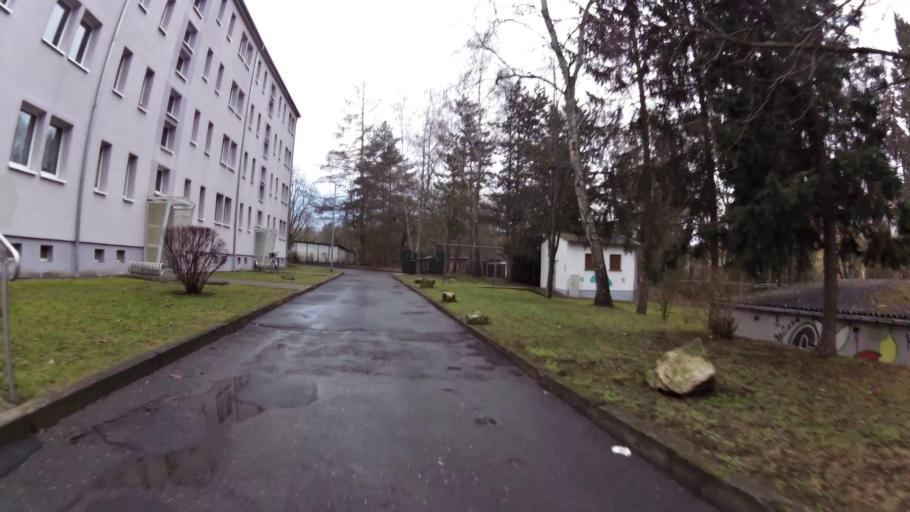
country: DE
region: Thuringia
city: Weimar
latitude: 50.9778
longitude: 11.3093
